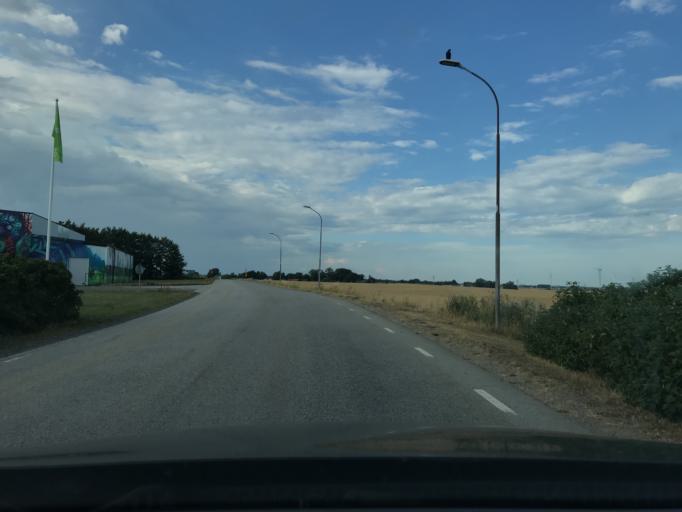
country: SE
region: Skane
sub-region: Simrishamns Kommun
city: Kivik
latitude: 55.5080
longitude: 14.1532
